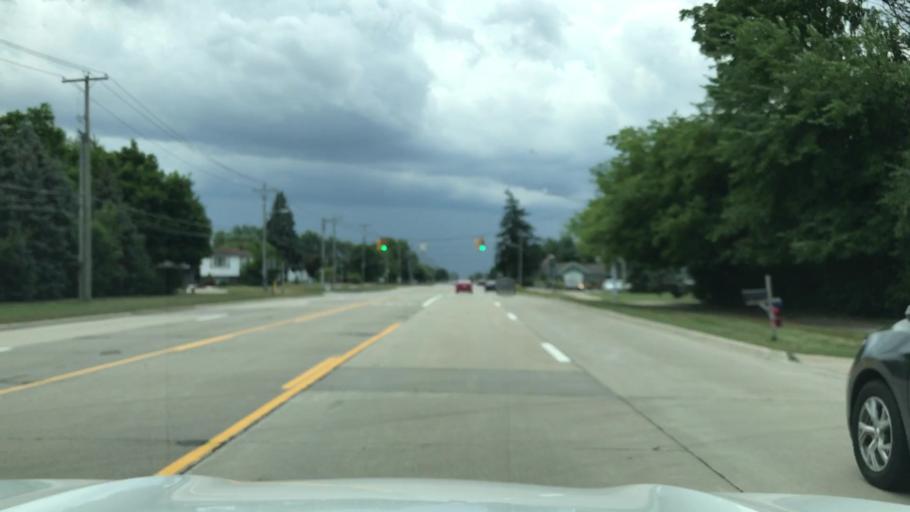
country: US
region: Michigan
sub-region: Oakland County
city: Clawson
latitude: 42.5698
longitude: -83.1085
